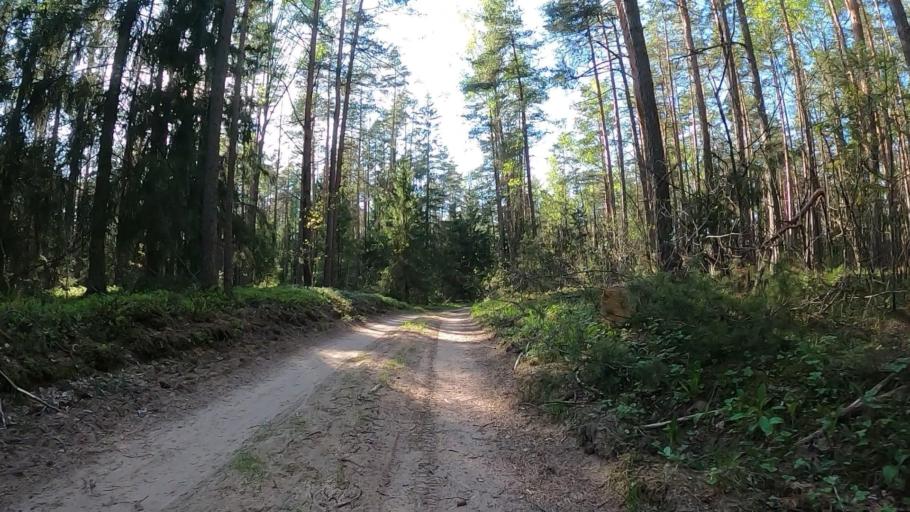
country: LV
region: Baldone
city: Baldone
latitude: 56.7661
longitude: 24.3694
